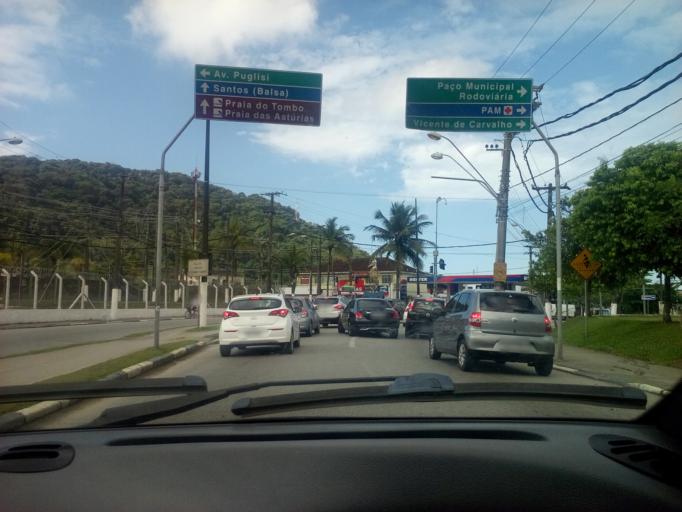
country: BR
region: Sao Paulo
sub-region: Guaruja
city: Guaruja
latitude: -23.9859
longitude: -46.2649
